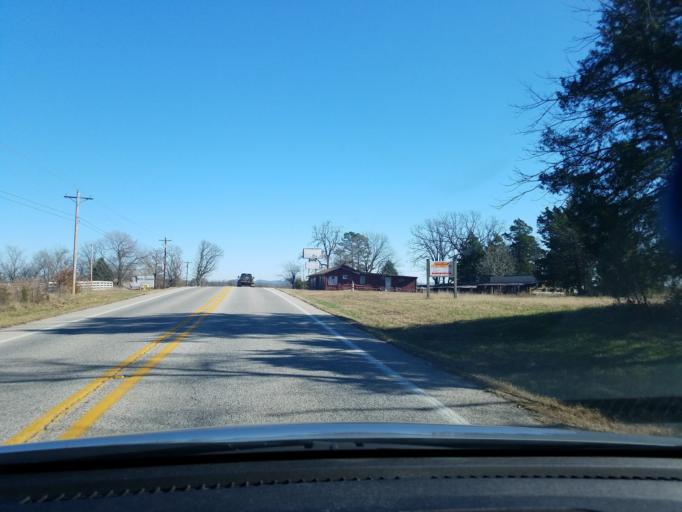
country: US
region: Arkansas
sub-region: Carroll County
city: Eureka Springs
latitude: 36.3980
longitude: -93.6555
